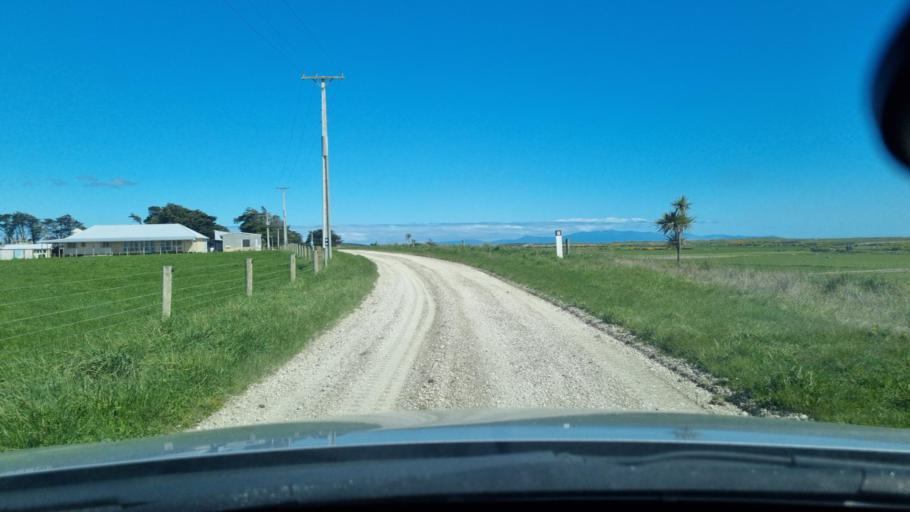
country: NZ
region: Southland
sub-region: Invercargill City
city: Invercargill
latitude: -46.3990
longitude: 168.2565
